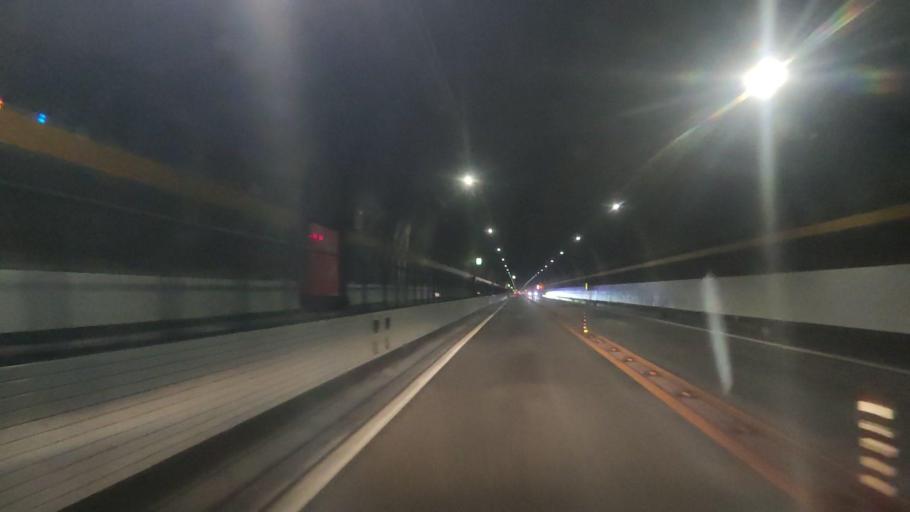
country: JP
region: Nagasaki
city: Obita
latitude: 32.7835
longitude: 129.8843
